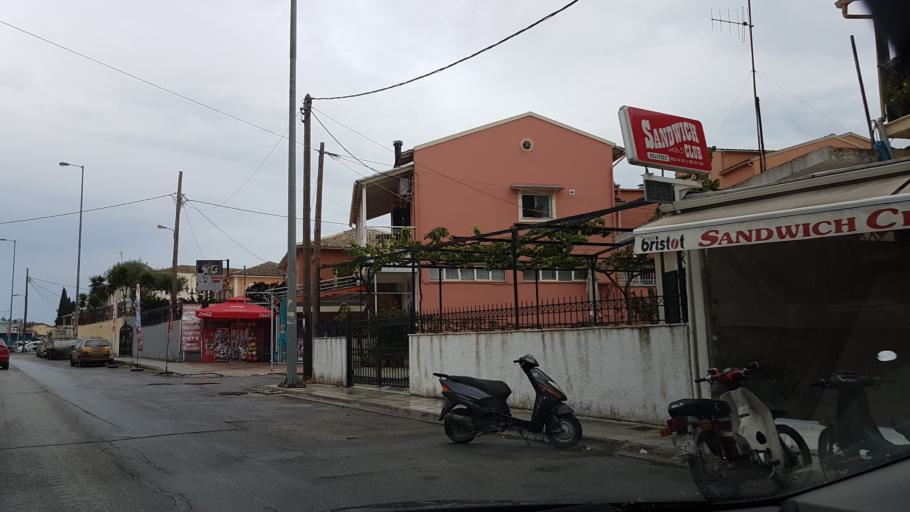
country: GR
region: Ionian Islands
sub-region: Nomos Kerkyras
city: Alepou
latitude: 39.6243
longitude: 19.8923
